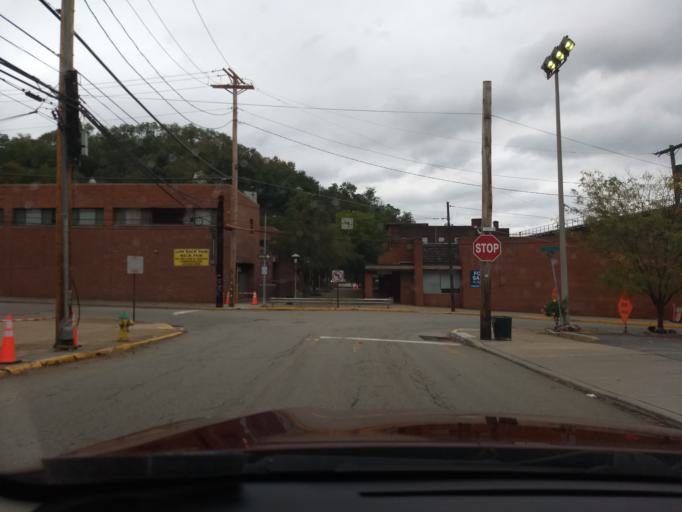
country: US
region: Pennsylvania
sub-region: Allegheny County
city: East Pittsburgh
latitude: 40.4000
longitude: -79.8354
